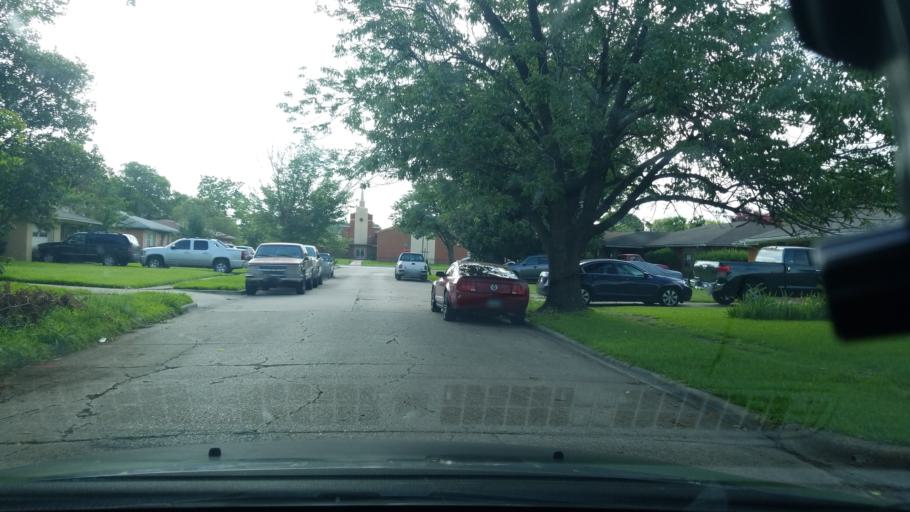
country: US
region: Texas
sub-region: Dallas County
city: Mesquite
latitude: 32.8178
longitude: -96.6696
